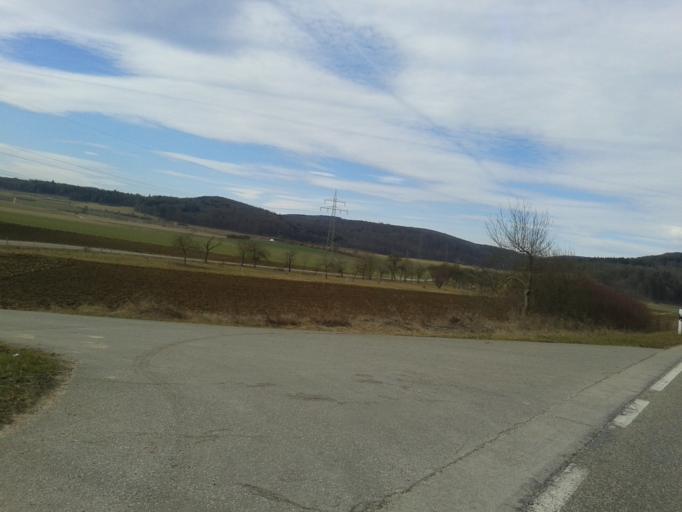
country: DE
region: Baden-Wuerttemberg
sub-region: Tuebingen Region
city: Altheim
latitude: 48.3500
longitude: 9.7551
